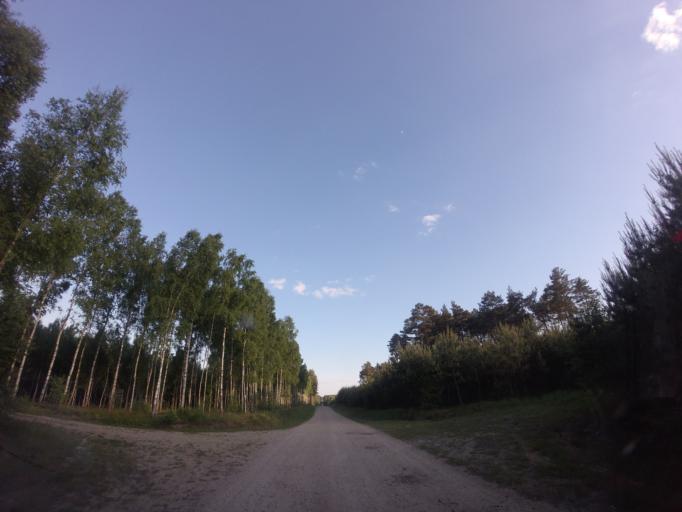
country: PL
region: West Pomeranian Voivodeship
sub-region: Powiat choszczenski
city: Drawno
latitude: 53.1515
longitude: 15.7292
